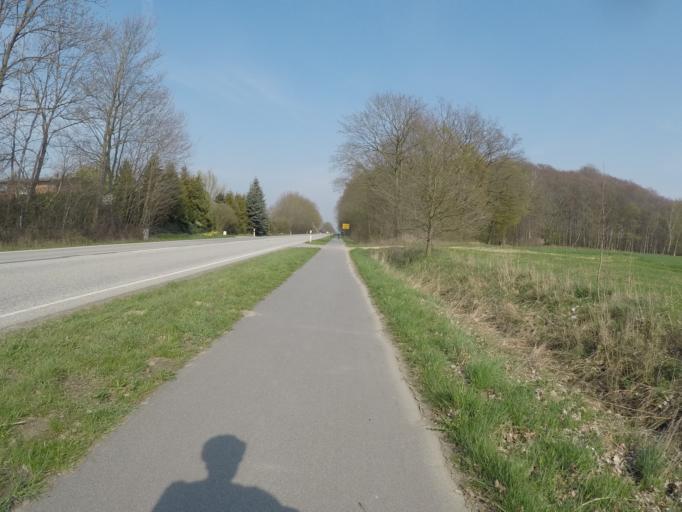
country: DE
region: Schleswig-Holstein
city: Seth
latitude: 53.8287
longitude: 10.2040
